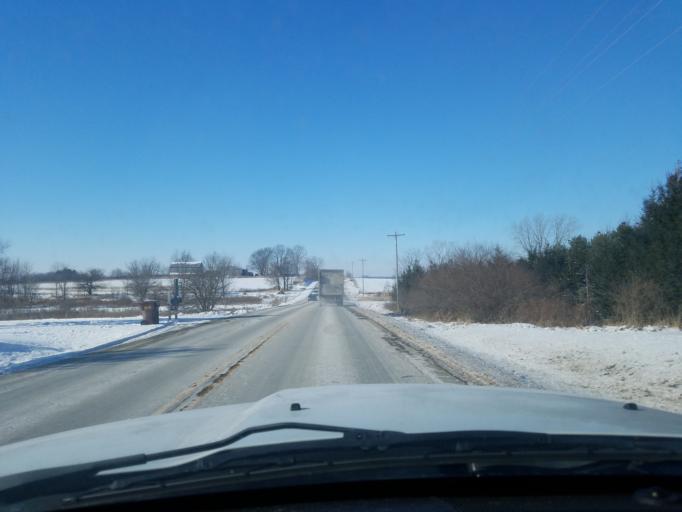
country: US
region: Indiana
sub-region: Noble County
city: Kendallville
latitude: 41.3947
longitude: -85.2966
